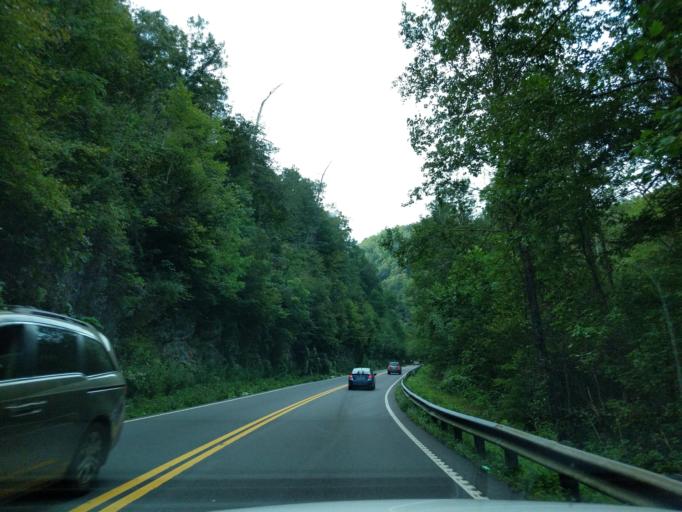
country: US
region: Tennessee
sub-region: Polk County
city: Benton
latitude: 35.1056
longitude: -84.5571
